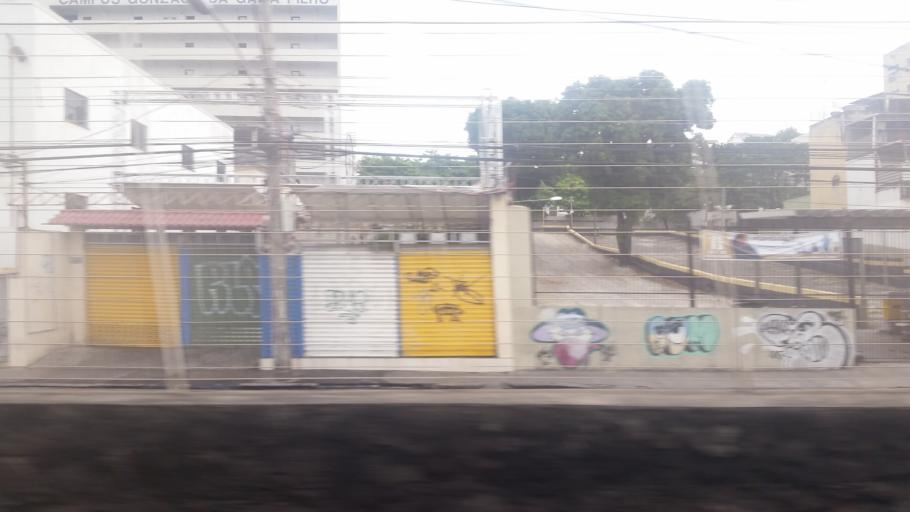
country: BR
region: Rio de Janeiro
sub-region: Rio De Janeiro
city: Rio de Janeiro
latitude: -22.8921
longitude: -43.3080
